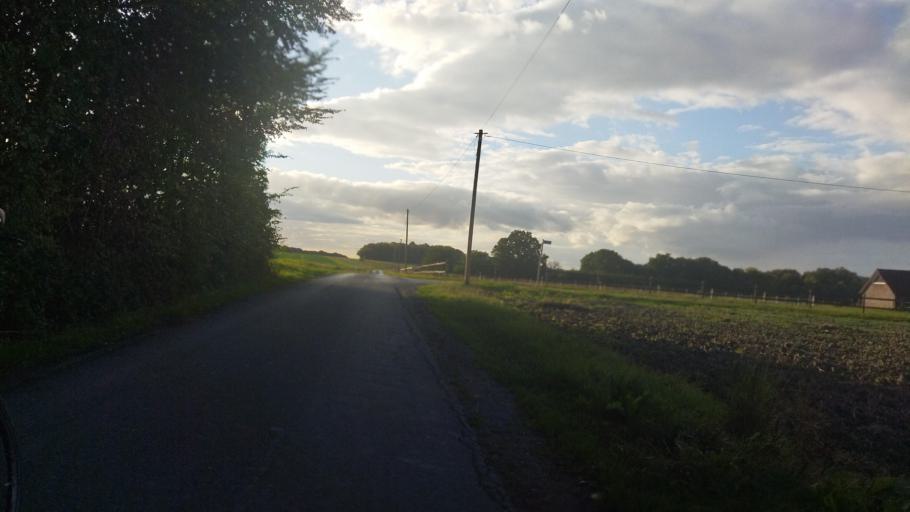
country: DE
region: North Rhine-Westphalia
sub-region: Regierungsbezirk Munster
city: Billerbeck
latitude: 51.9577
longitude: 7.2629
